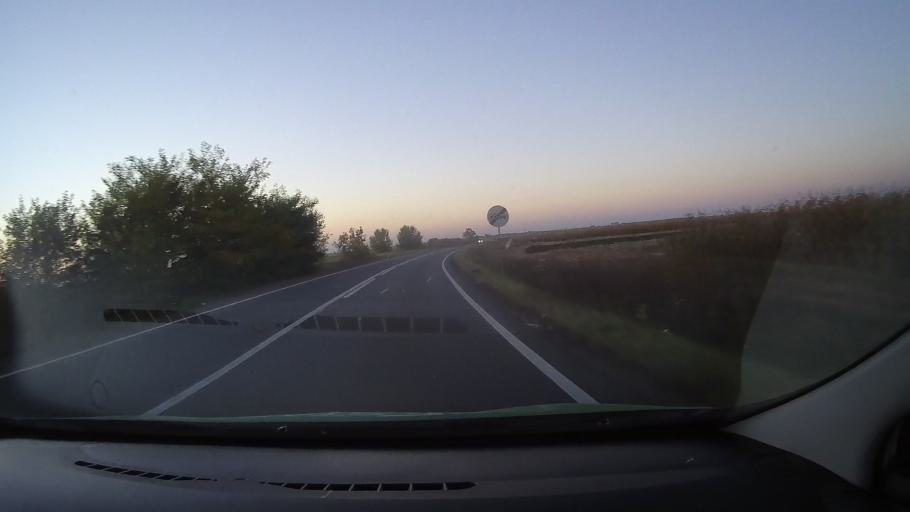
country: RO
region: Bihor
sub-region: Comuna Tarcea
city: Tarcea
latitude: 47.4400
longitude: 22.1934
